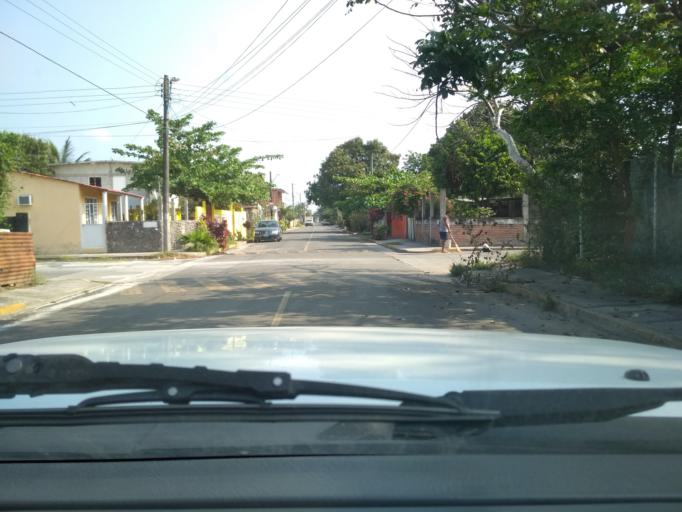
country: MX
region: Veracruz
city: El Tejar
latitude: 19.0795
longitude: -96.1606
